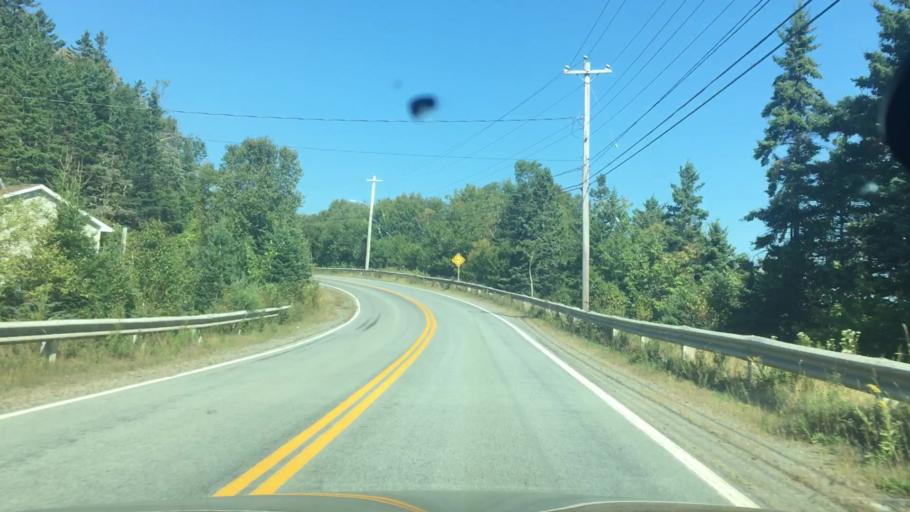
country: CA
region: Nova Scotia
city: New Glasgow
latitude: 44.9164
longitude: -62.5389
